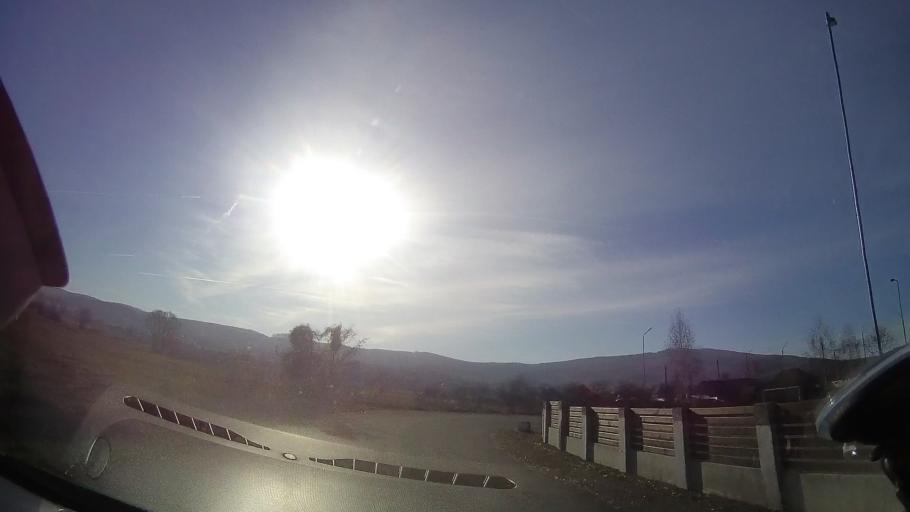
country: RO
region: Bihor
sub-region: Comuna Magesti
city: Magesti
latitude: 47.0119
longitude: 22.4558
